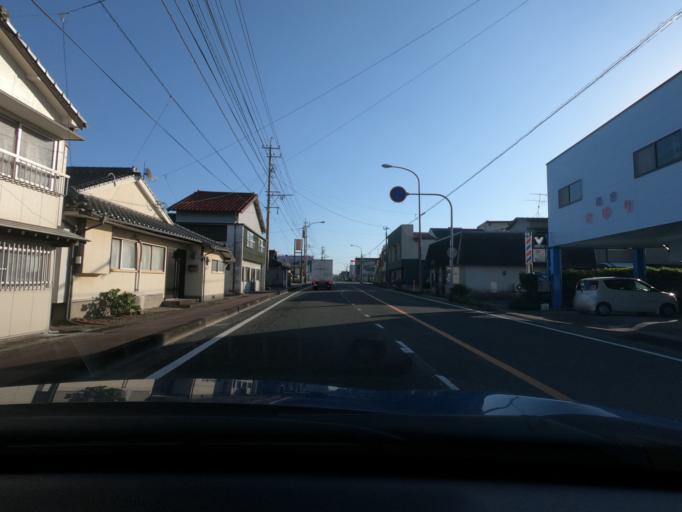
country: JP
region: Kagoshima
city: Akune
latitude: 32.0239
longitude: 130.1957
